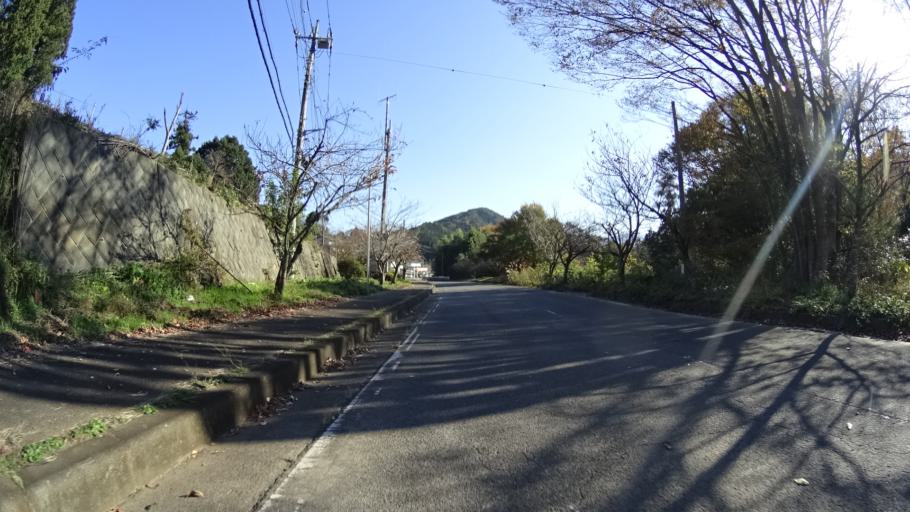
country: JP
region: Yamanashi
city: Uenohara
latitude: 35.6450
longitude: 139.1257
